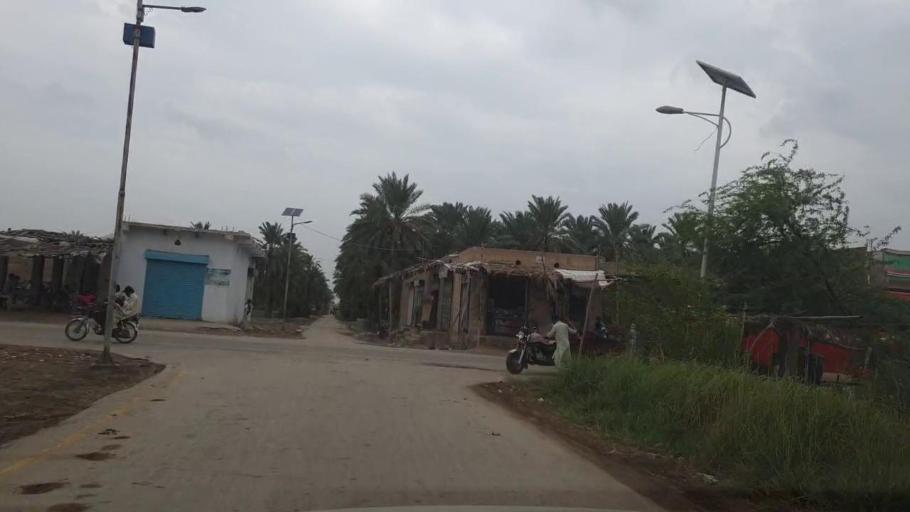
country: PK
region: Sindh
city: Khairpur
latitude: 27.5526
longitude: 68.7508
